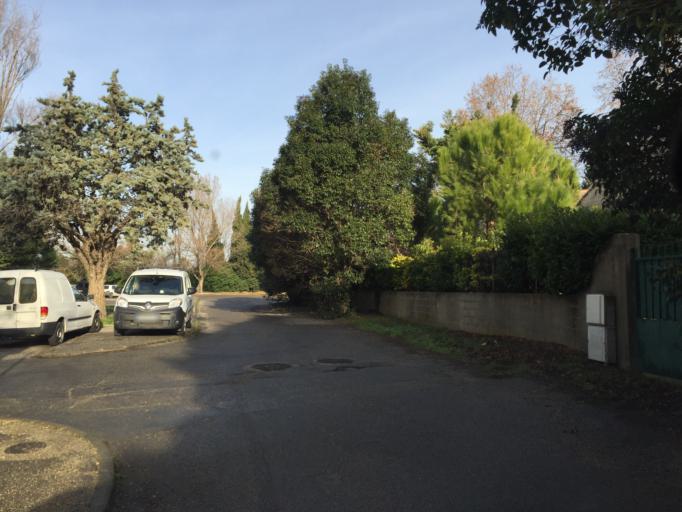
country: FR
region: Provence-Alpes-Cote d'Azur
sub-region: Departement du Vaucluse
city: Orange
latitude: 44.1550
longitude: 4.8013
